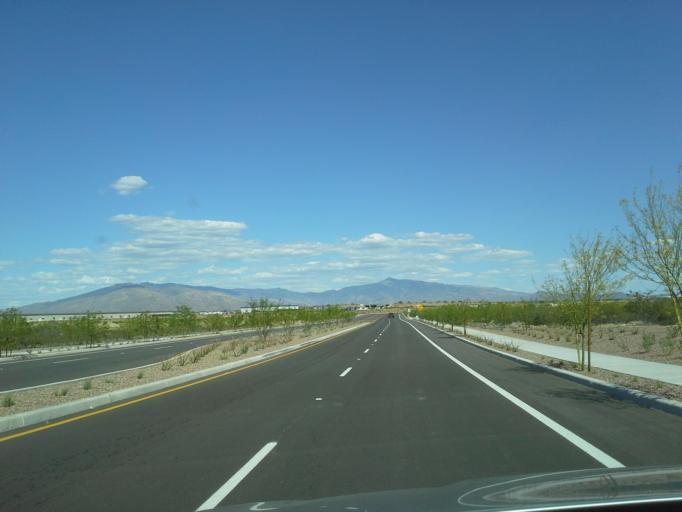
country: US
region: Arizona
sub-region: Pima County
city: Summit
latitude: 32.1199
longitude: -110.8574
